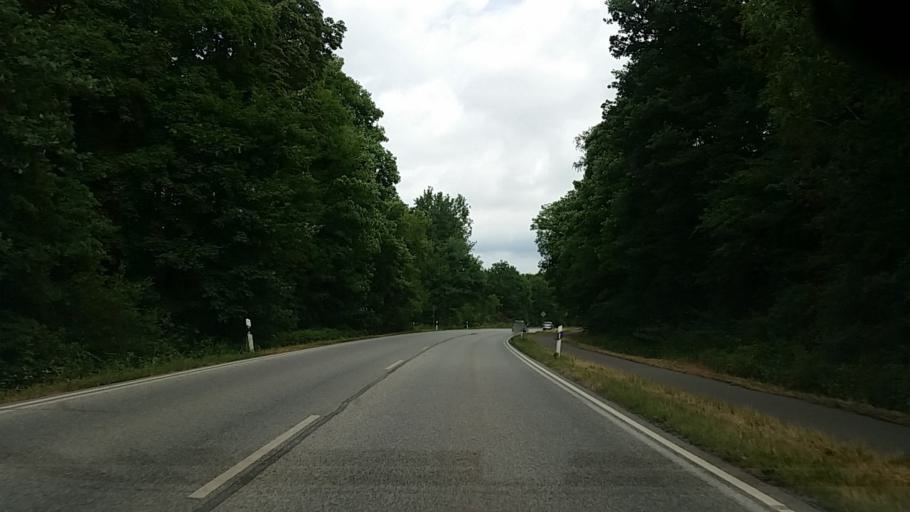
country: DE
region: Schleswig-Holstein
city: Kayhude
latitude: 53.7440
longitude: 10.1215
